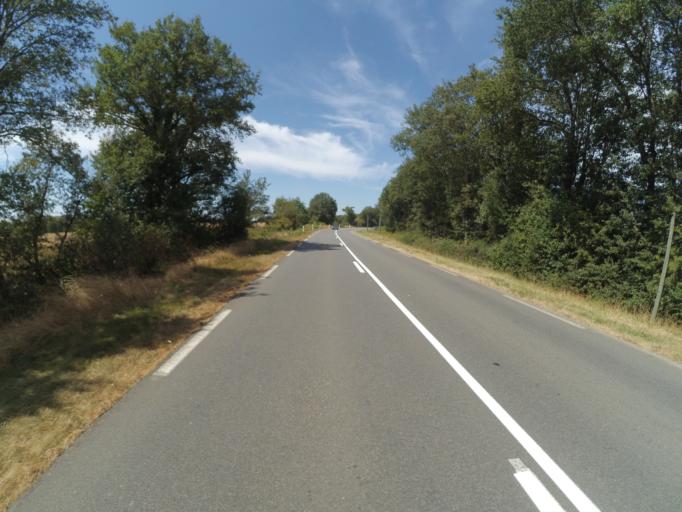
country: FR
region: Poitou-Charentes
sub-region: Departement de la Vienne
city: Availles-Limouzine
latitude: 46.0703
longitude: 0.5944
